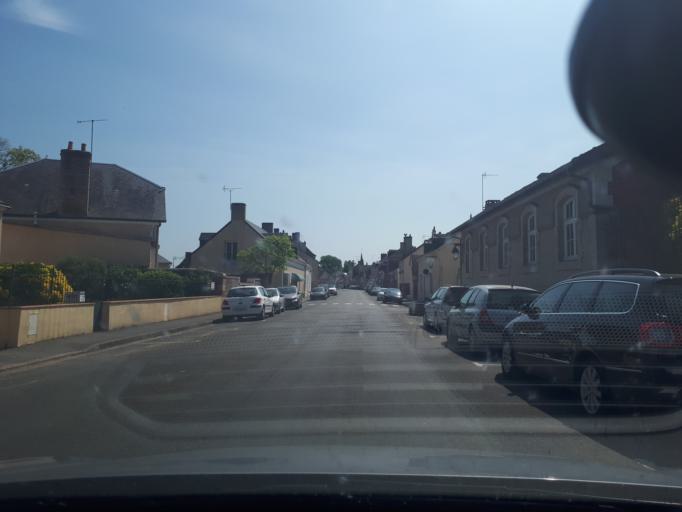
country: FR
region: Pays de la Loire
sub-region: Departement de la Sarthe
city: Montfort-le-Gesnois
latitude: 48.0485
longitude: 0.4117
